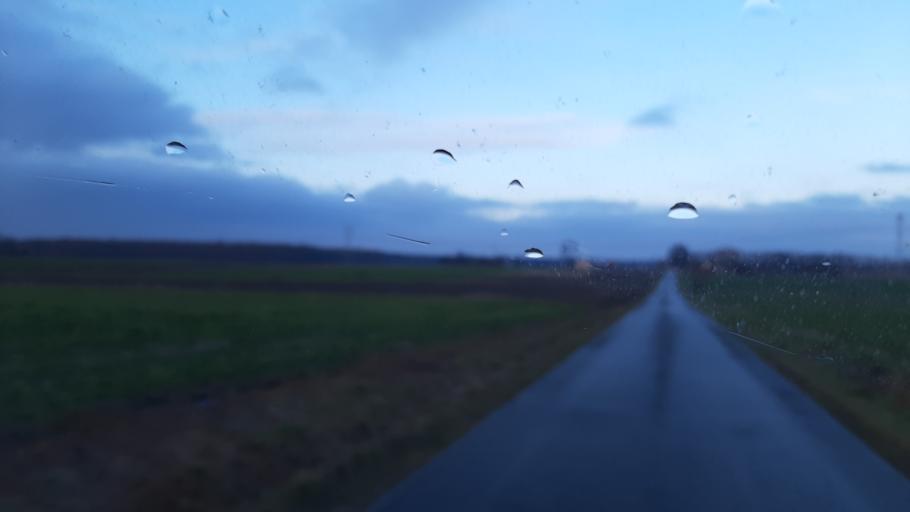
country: PL
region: Lublin Voivodeship
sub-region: Powiat lubelski
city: Garbow
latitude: 51.3613
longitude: 22.3967
